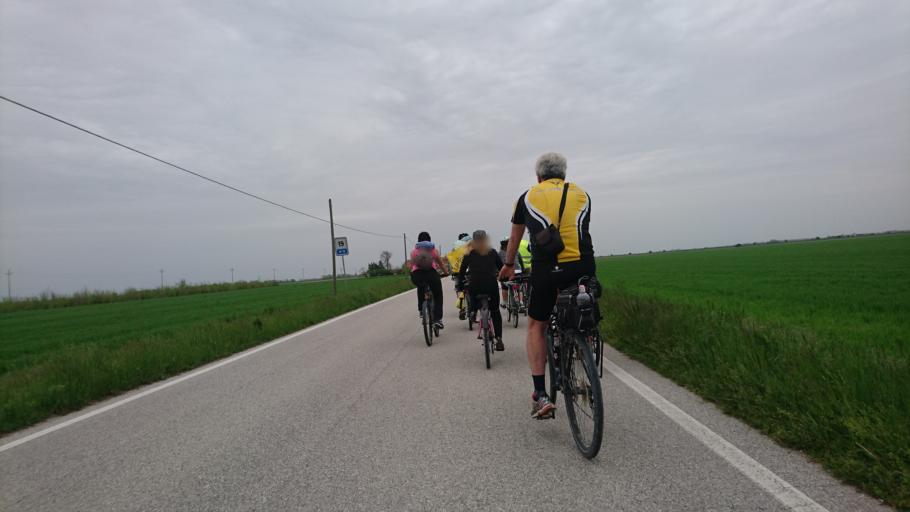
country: IT
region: Veneto
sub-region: Provincia di Venezia
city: Lugugnana
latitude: 45.6642
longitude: 12.9473
